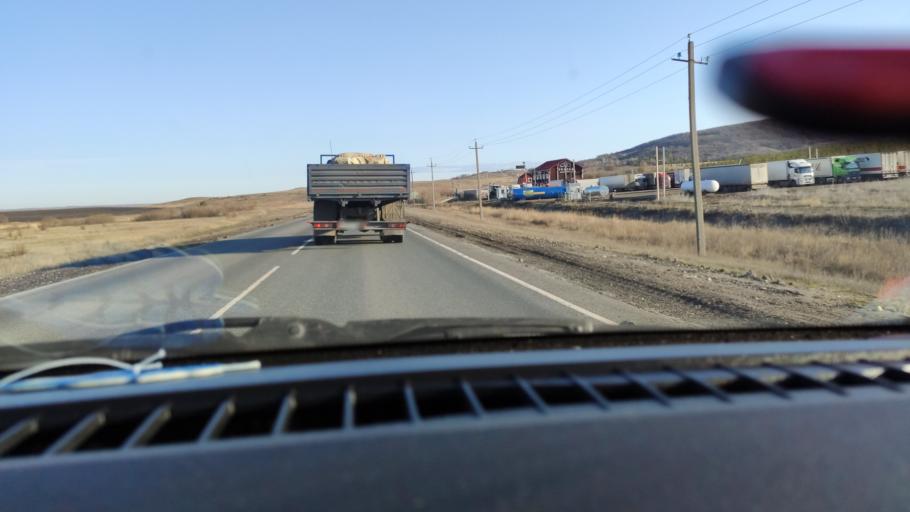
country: RU
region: Saratov
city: Alekseyevka
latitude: 52.3075
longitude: 47.9252
